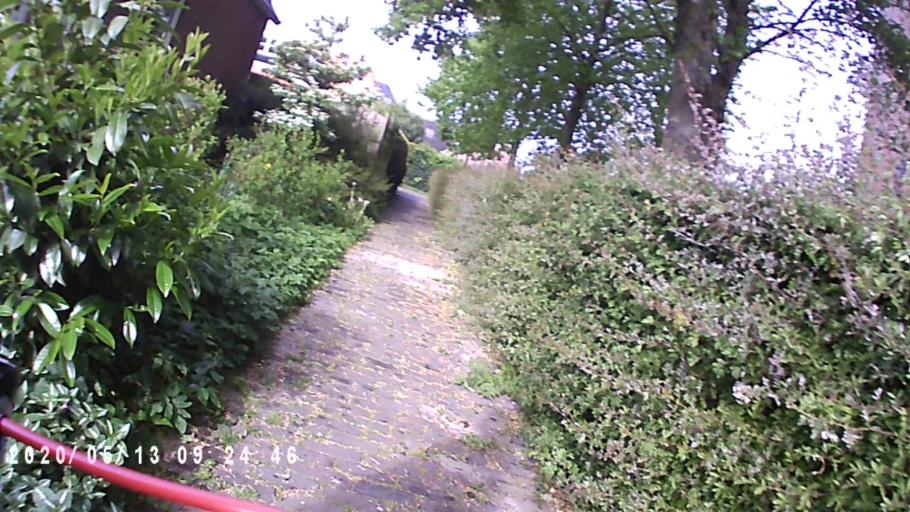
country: NL
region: Groningen
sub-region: Gemeente Zuidhorn
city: Noordhorn
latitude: 53.2608
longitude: 6.3960
